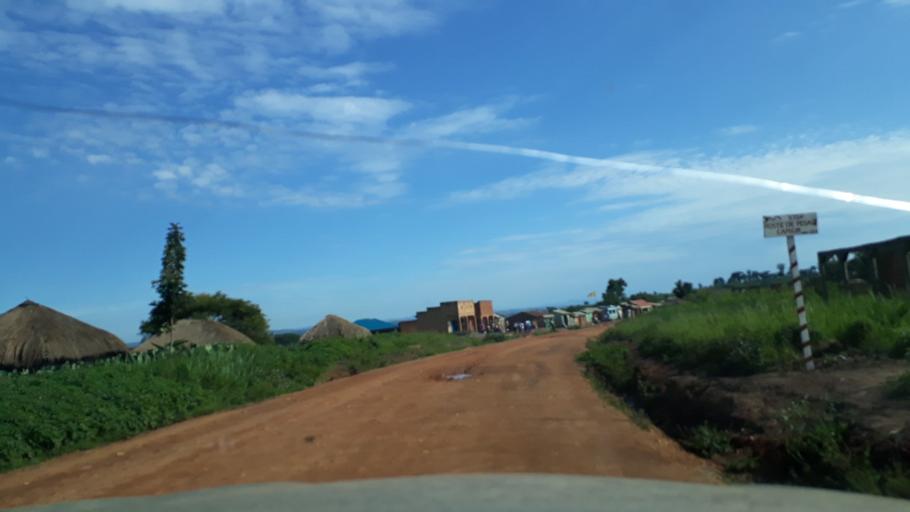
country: UG
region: Northern Region
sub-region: Zombo District
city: Paidha
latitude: 2.3412
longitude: 31.0252
